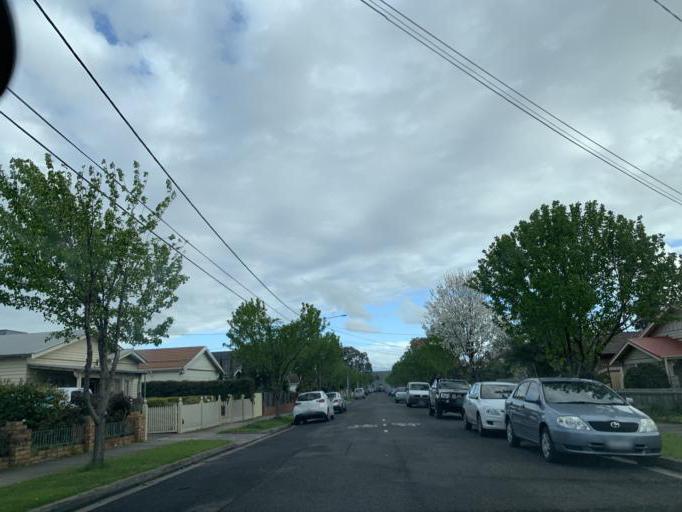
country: AU
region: Victoria
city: Thornbury
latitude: -37.7459
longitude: 144.9943
